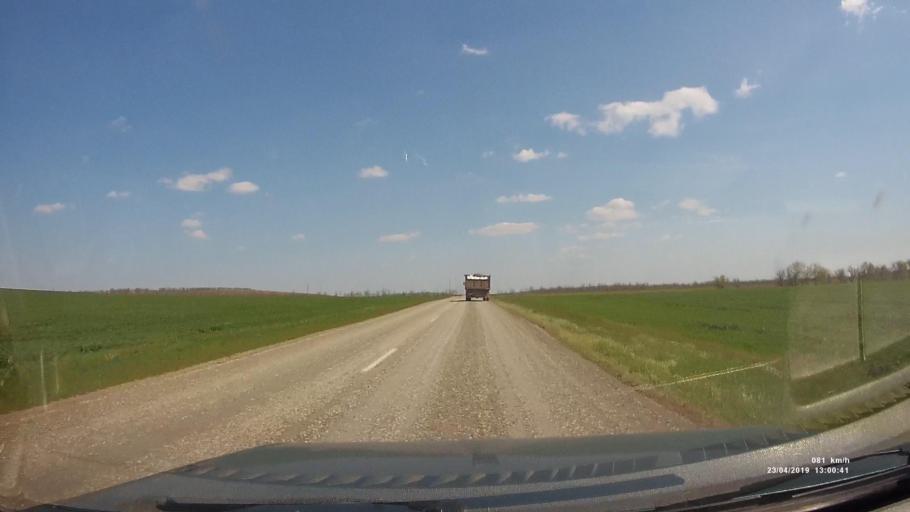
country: RU
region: Kalmykiya
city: Yashalta
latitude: 46.6040
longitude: 42.6400
